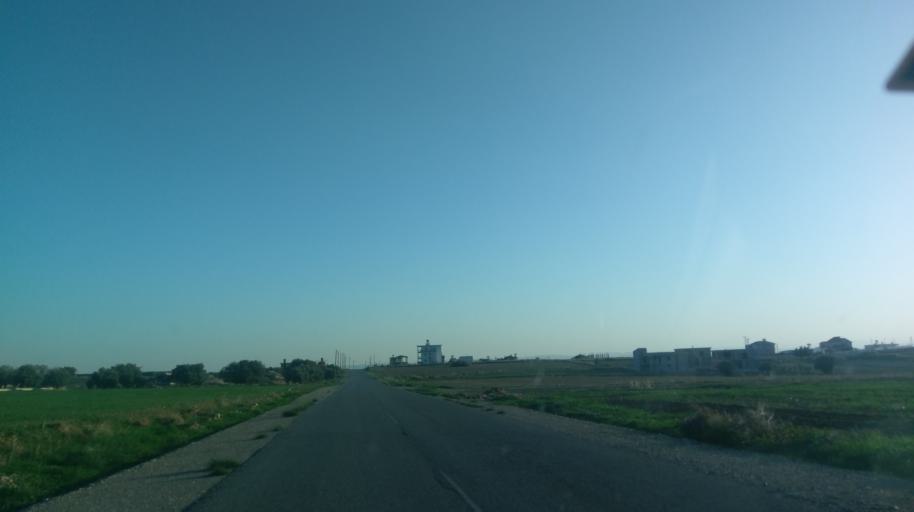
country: CY
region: Ammochostos
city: Lefkonoiko
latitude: 35.2443
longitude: 33.5535
